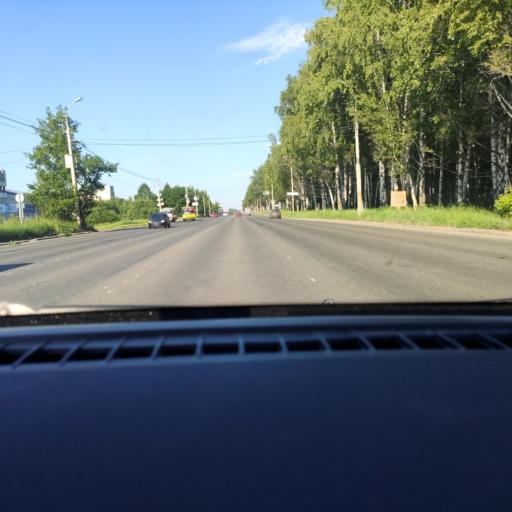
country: RU
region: Udmurtiya
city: Khokhryaki
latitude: 56.9068
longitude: 53.3498
